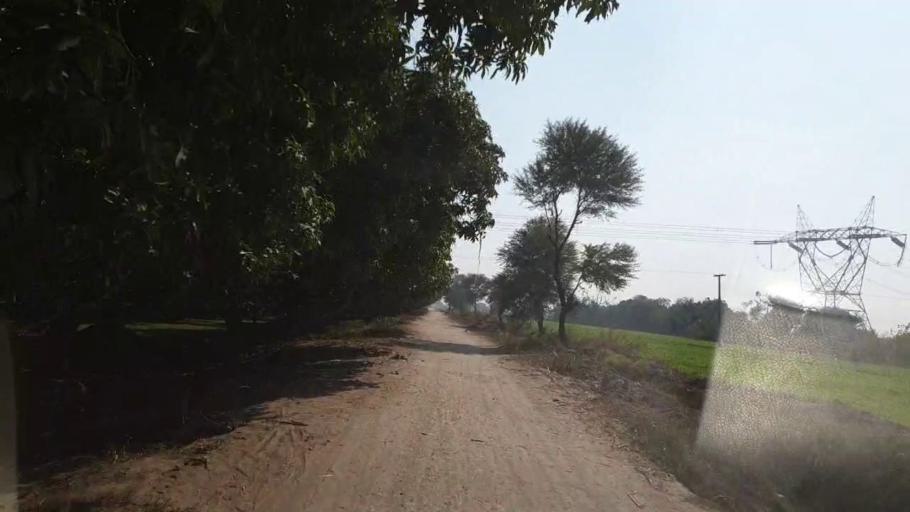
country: PK
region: Sindh
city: Matiari
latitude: 25.5142
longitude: 68.4596
